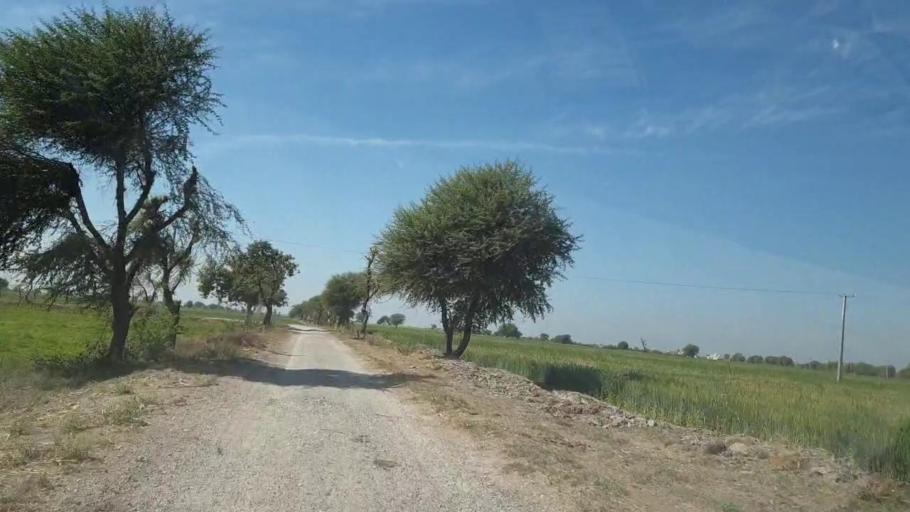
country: PK
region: Sindh
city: Pithoro
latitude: 25.6256
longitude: 69.2564
